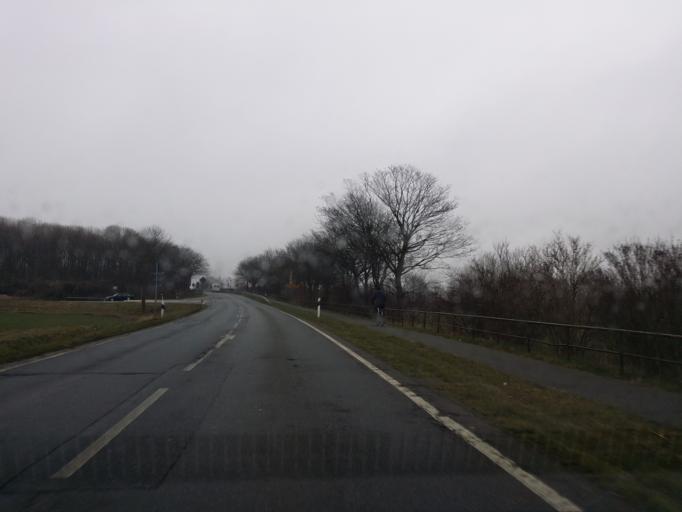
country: DE
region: Schleswig-Holstein
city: Fehmarn
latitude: 54.4462
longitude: 11.1662
